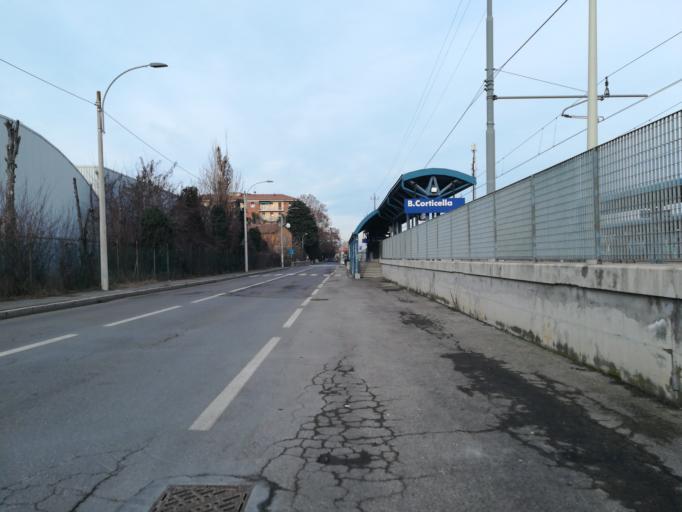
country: IT
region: Emilia-Romagna
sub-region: Provincia di Bologna
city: Progresso
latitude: 44.5518
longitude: 11.3536
